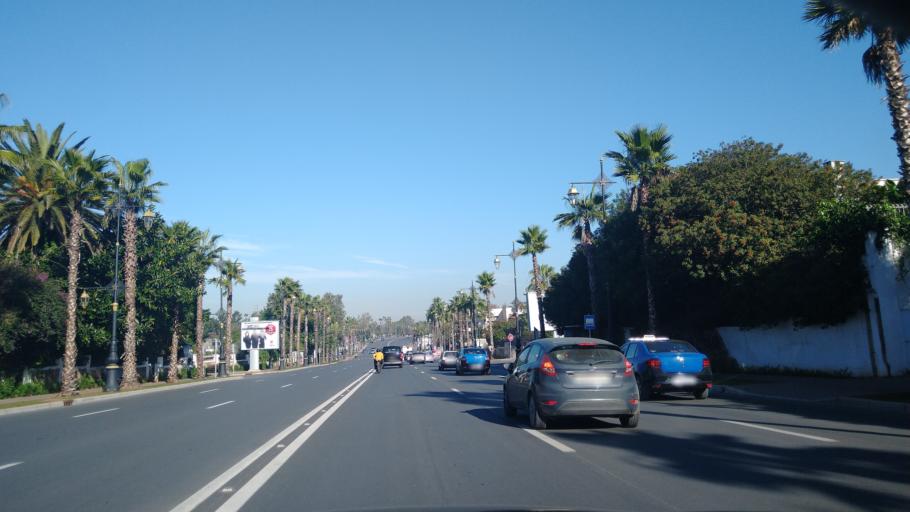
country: MA
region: Rabat-Sale-Zemmour-Zaer
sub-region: Rabat
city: Rabat
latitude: 33.9975
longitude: -6.8274
